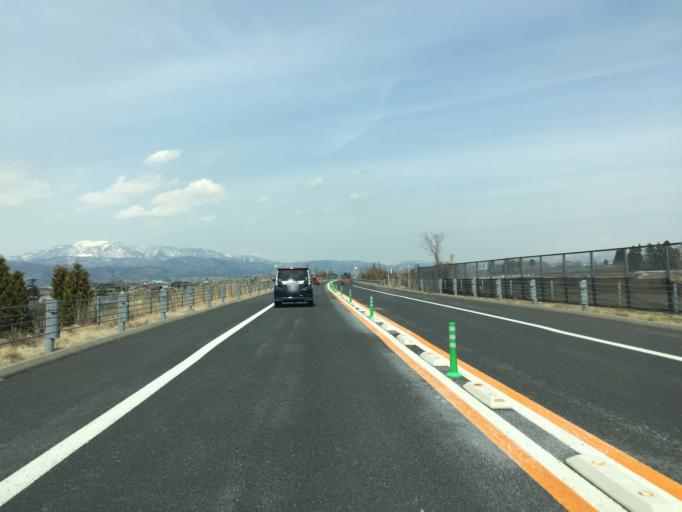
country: JP
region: Yamagata
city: Tendo
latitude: 38.3881
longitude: 140.3438
